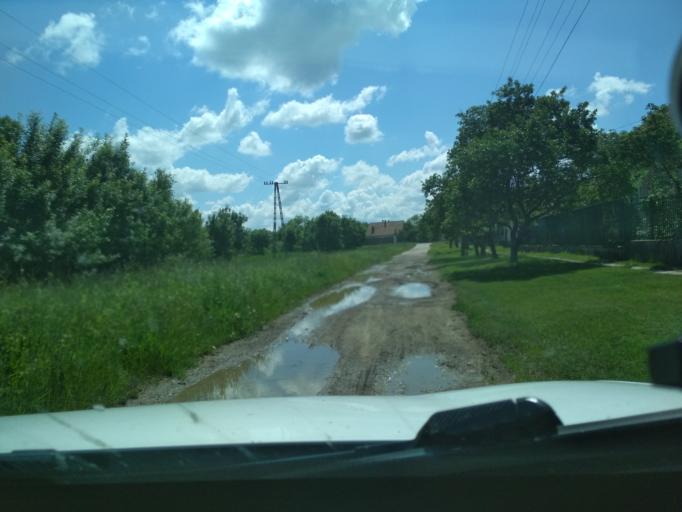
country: HU
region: Jasz-Nagykun-Szolnok
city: Abadszalok
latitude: 47.4830
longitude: 20.6049
